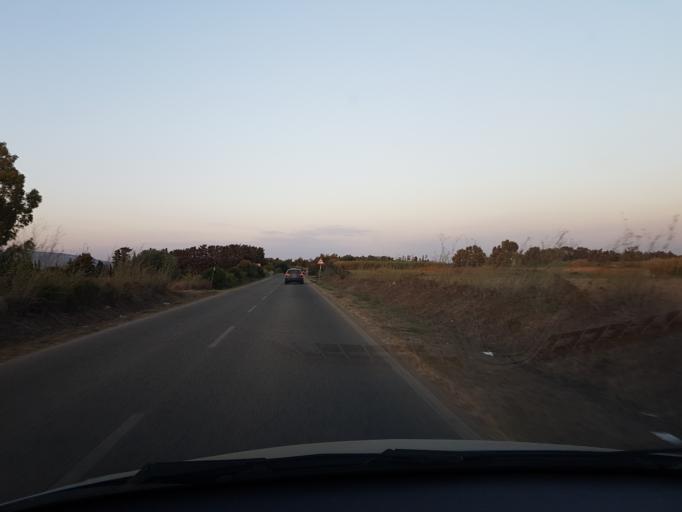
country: IT
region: Sardinia
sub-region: Provincia di Oristano
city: Riola Sardo
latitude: 39.9937
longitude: 8.4699
